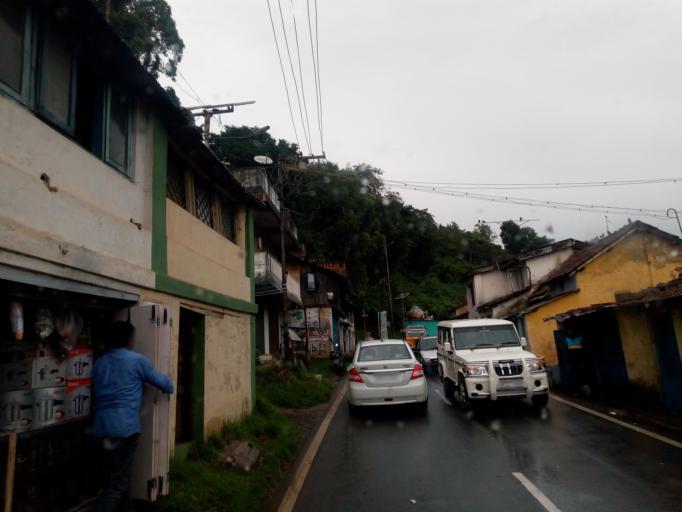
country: IN
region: Tamil Nadu
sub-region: Nilgiri
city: Wellington
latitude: 11.3558
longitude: 76.7842
